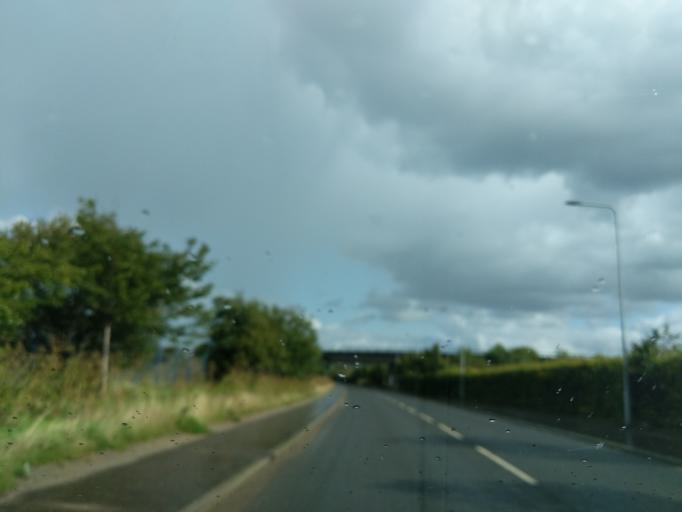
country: GB
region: Scotland
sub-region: Fife
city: Rosyth
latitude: 56.0218
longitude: -3.4238
